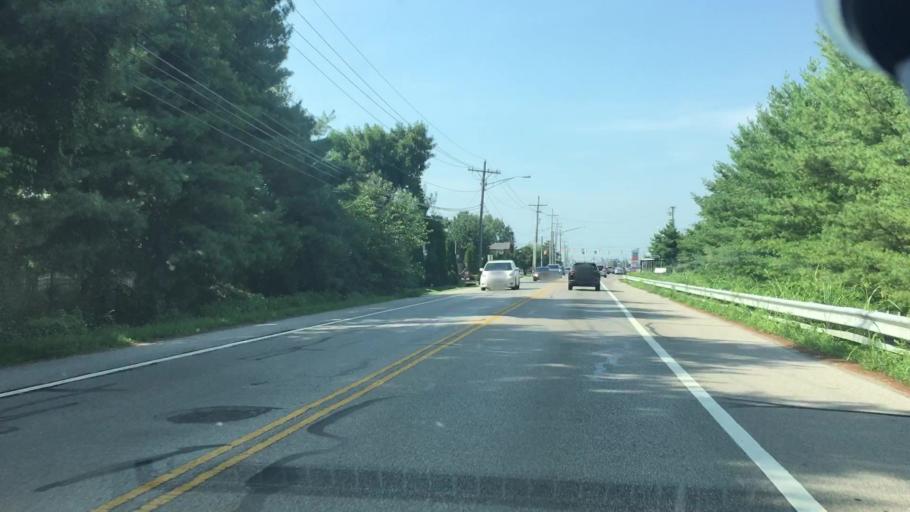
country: US
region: Indiana
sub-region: Vanderburgh County
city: Melody Hill
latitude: 37.9722
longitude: -87.4743
